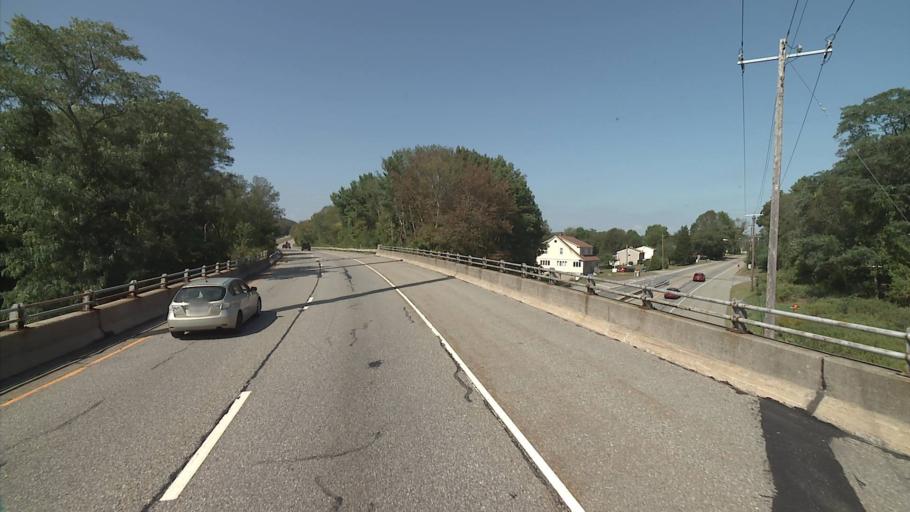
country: US
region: Connecticut
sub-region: New London County
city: Uncasville
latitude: 41.4184
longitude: -72.1101
